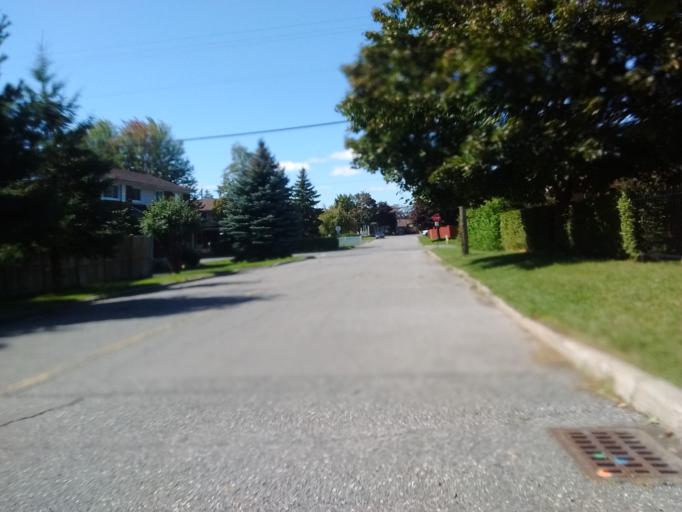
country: CA
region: Ontario
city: Ottawa
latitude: 45.4375
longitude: -75.6380
